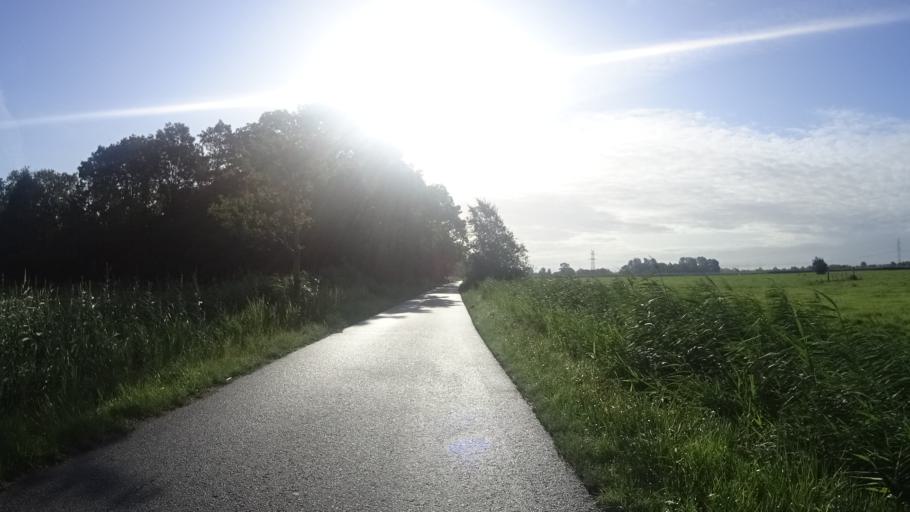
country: DE
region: Lower Saxony
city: Nordenham
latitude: 53.4973
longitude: 8.4260
